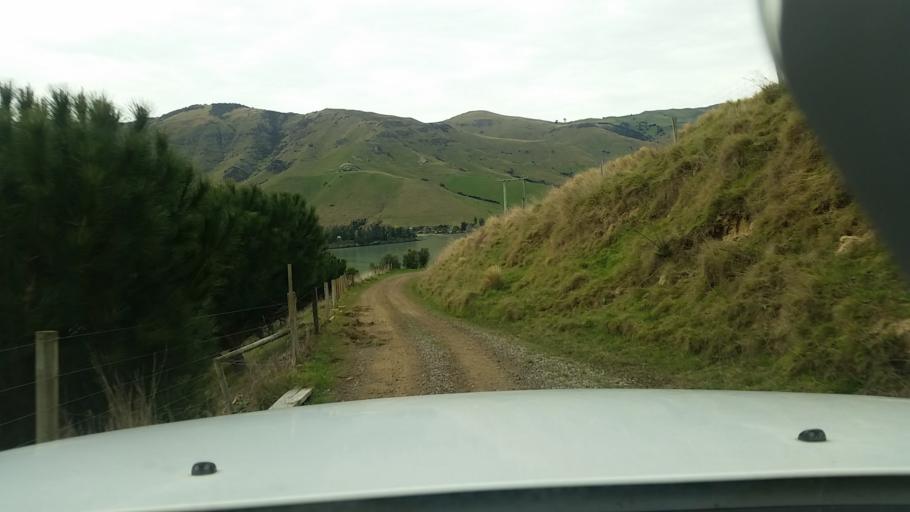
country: NZ
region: Canterbury
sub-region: Christchurch City
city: Christchurch
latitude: -43.6442
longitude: 172.8178
